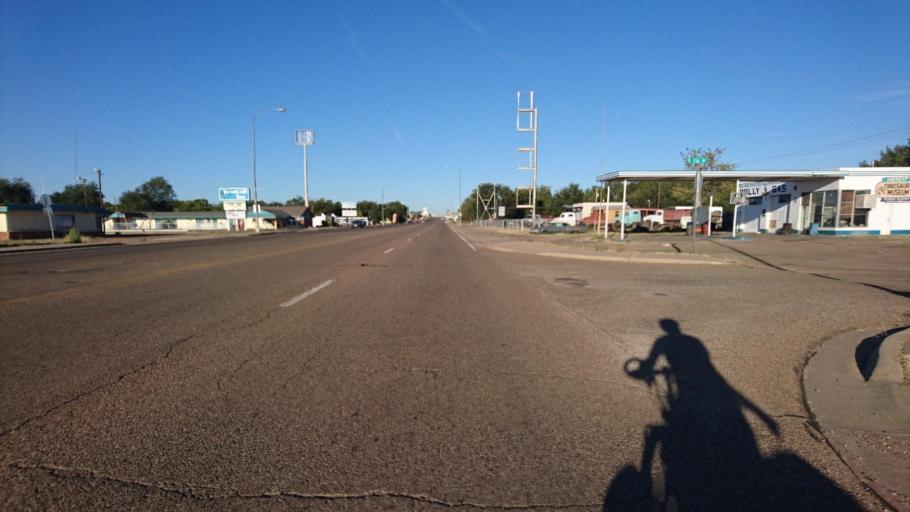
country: US
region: New Mexico
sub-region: Quay County
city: Tucumcari
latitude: 35.1719
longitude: -103.7040
